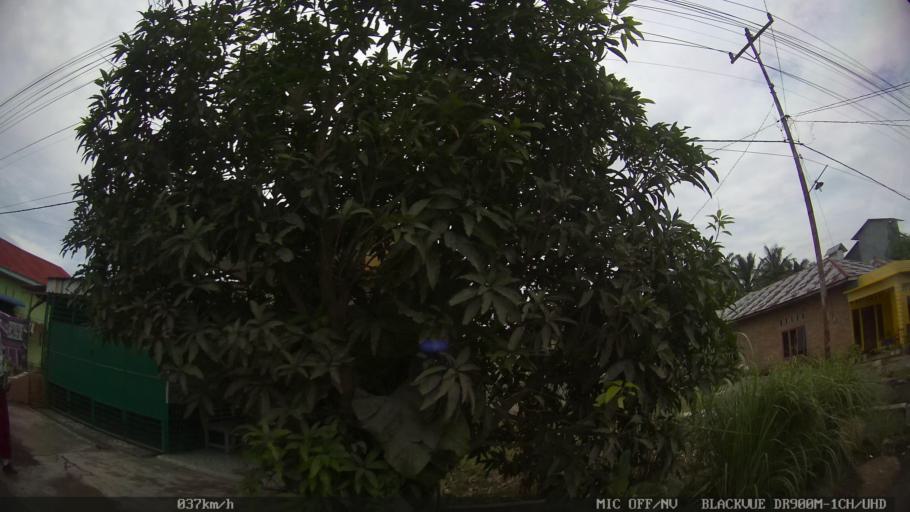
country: ID
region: North Sumatra
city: Binjai
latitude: 3.6290
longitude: 98.5568
